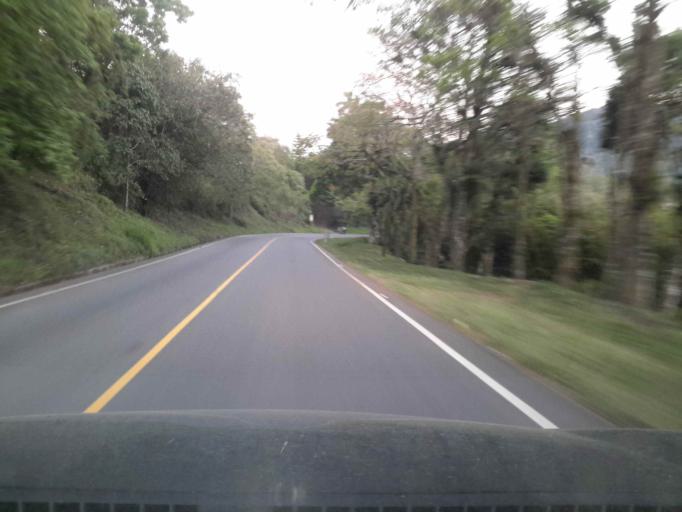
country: NI
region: Matagalpa
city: Matagalpa
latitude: 13.0008
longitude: -85.9231
